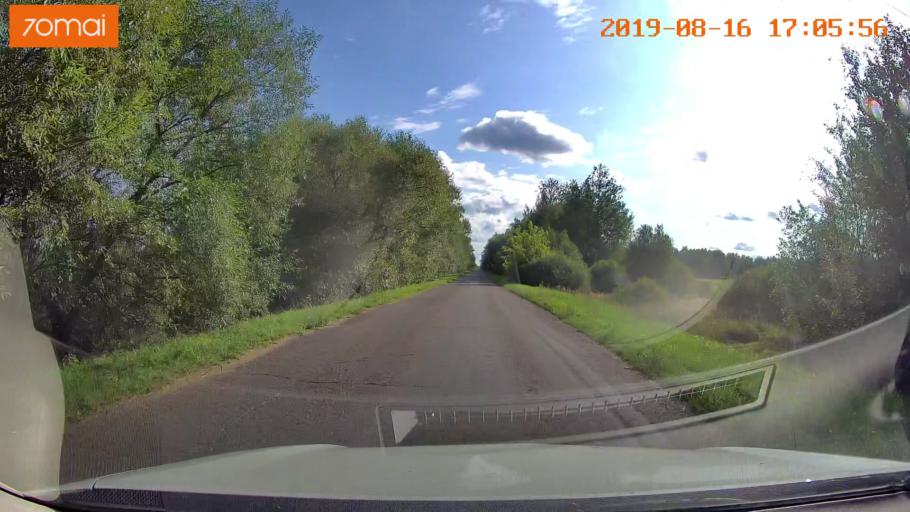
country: BY
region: Mogilev
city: Hlusha
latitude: 53.2324
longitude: 28.9388
